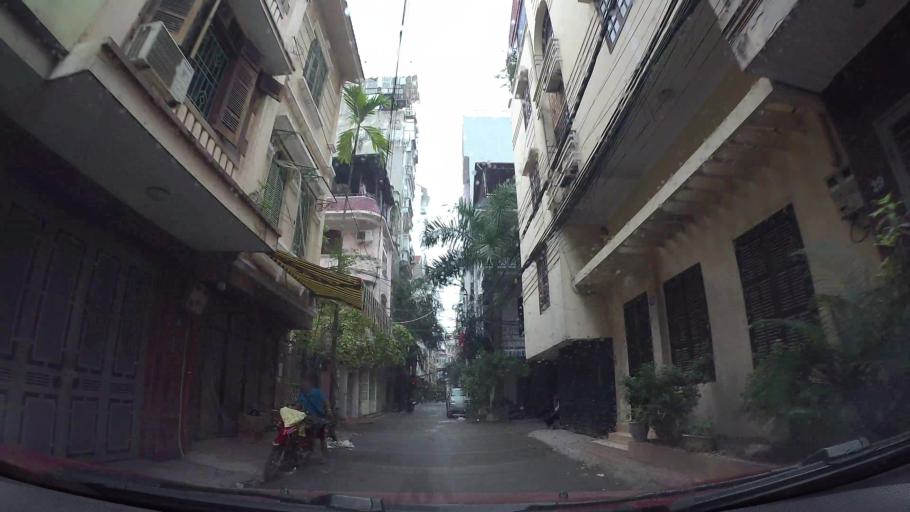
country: VN
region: Ha Noi
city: Dong Da
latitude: 21.0156
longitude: 105.8259
